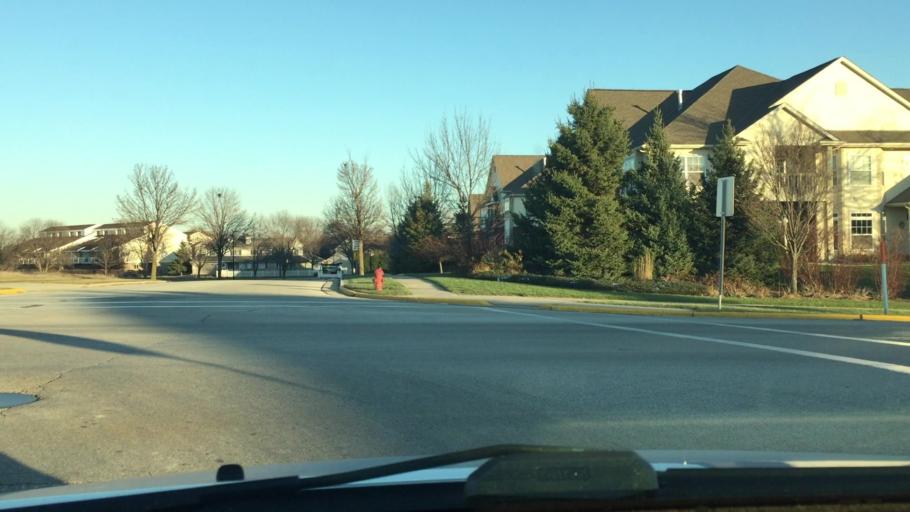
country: US
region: Wisconsin
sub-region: Waukesha County
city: Pewaukee
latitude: 43.0911
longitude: -88.2751
